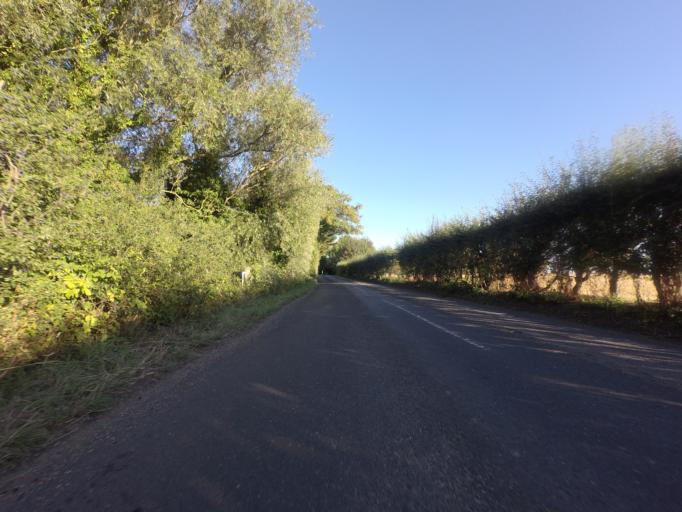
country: GB
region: England
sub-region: Kent
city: Herne Bay
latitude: 51.3446
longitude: 1.1876
